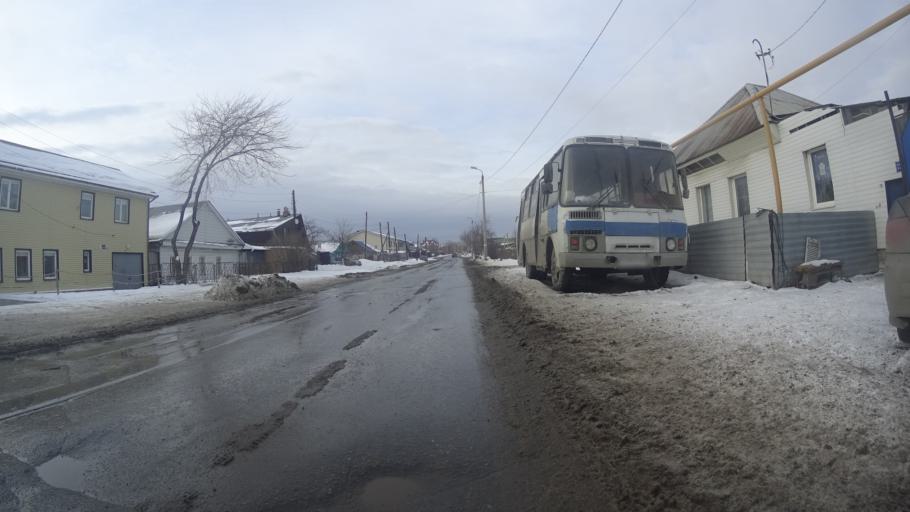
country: RU
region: Chelyabinsk
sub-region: Gorod Chelyabinsk
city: Chelyabinsk
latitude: 55.1291
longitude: 61.3915
